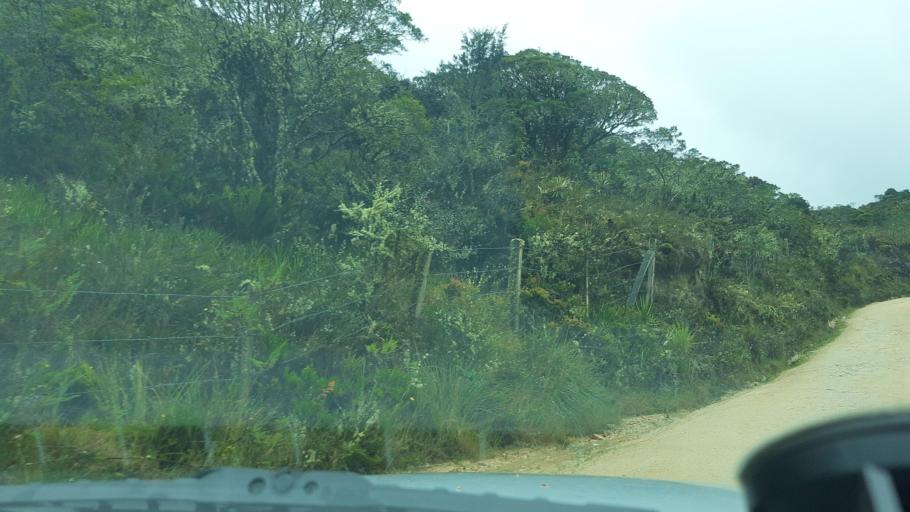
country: CO
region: Cundinamarca
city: Villapinzon
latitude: 5.2059
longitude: -73.5523
